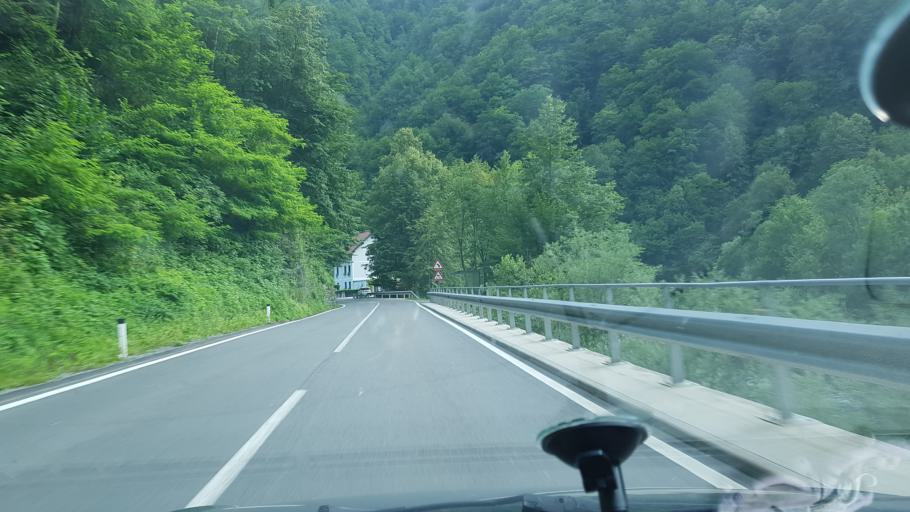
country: SI
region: Idrija
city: Spodnja Idrija
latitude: 46.0563
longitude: 14.0182
